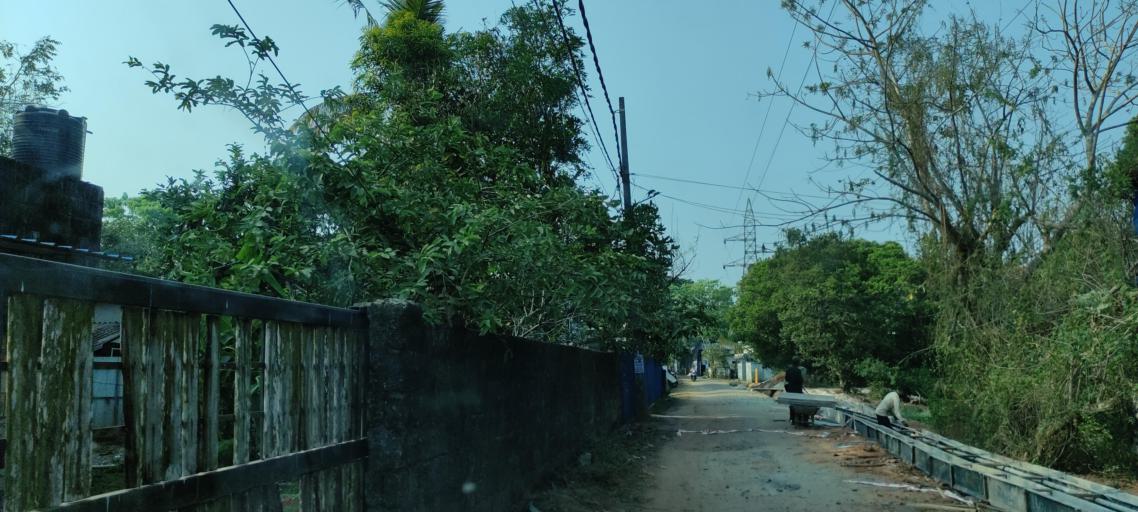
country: IN
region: Kerala
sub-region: Alappuzha
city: Alleppey
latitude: 9.5256
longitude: 76.3217
